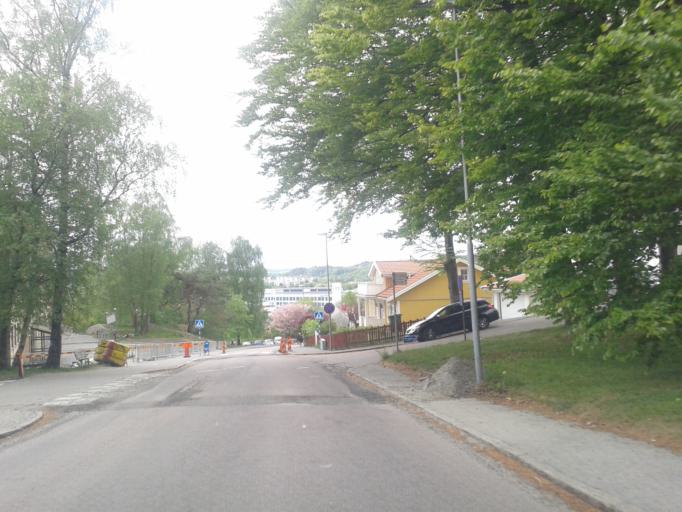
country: SE
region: Vaestra Goetaland
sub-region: Kungalvs Kommun
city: Kungalv
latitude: 57.8710
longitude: 11.9866
